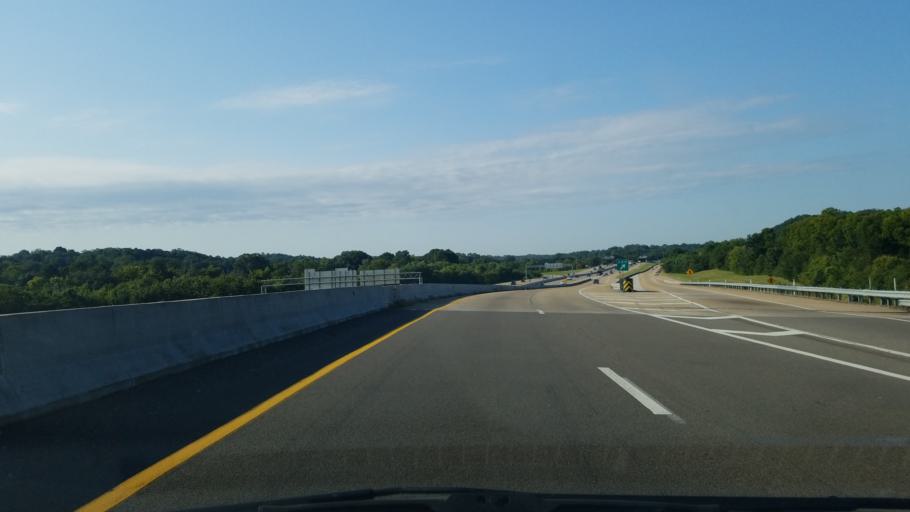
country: US
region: Tennessee
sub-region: Hamilton County
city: East Brainerd
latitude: 35.0249
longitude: -85.1745
